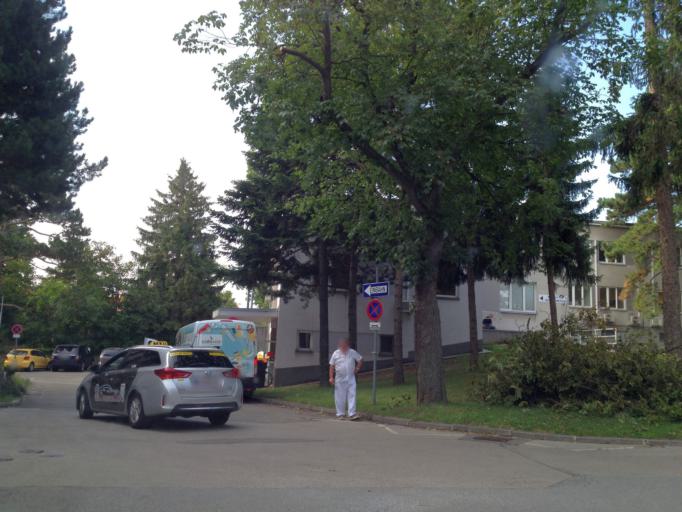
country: AT
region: Lower Austria
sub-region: Politischer Bezirk Modling
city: Perchtoldsdorf
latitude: 48.1680
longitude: 16.2765
